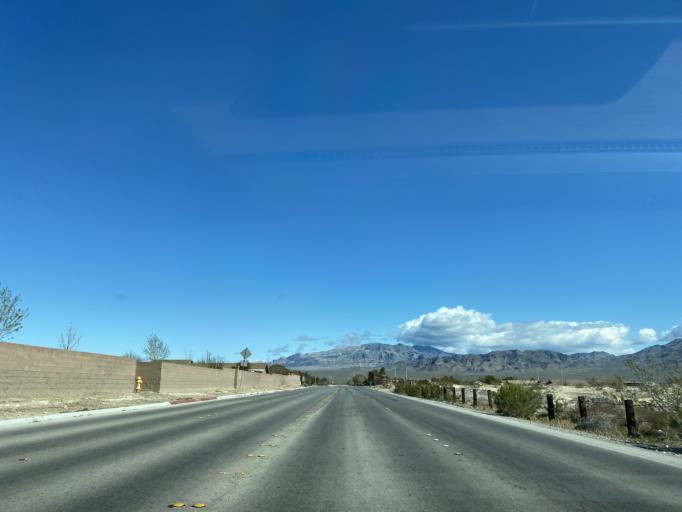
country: US
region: Nevada
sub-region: Clark County
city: North Las Vegas
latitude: 36.3269
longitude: -115.2785
